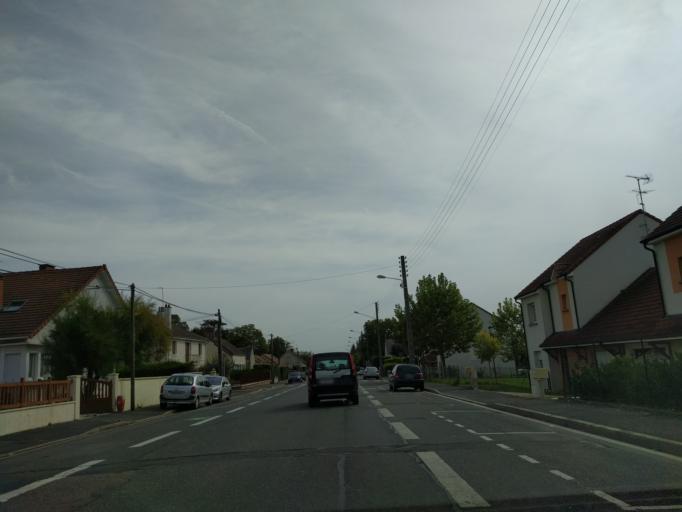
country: FR
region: Centre
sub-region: Departement du Cher
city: Bourges
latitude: 47.0617
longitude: 2.4230
